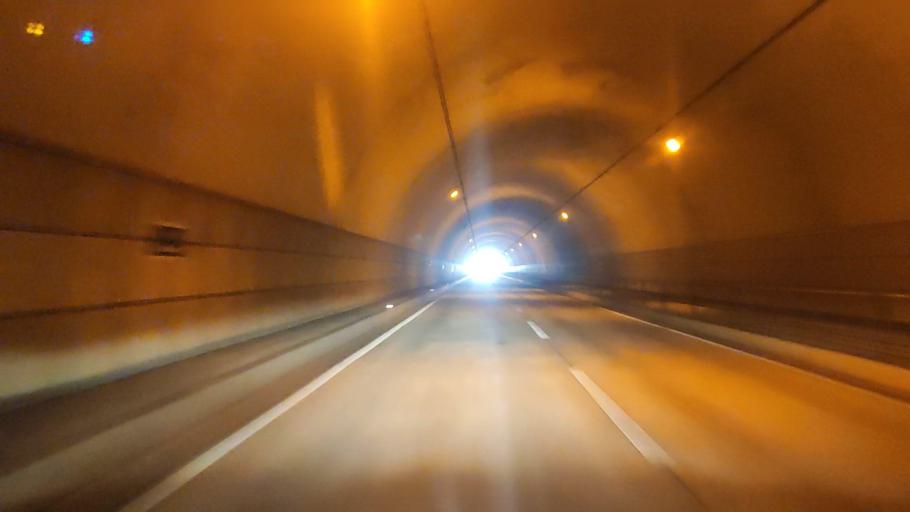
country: JP
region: Miyazaki
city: Nobeoka
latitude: 32.6863
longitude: 131.7943
